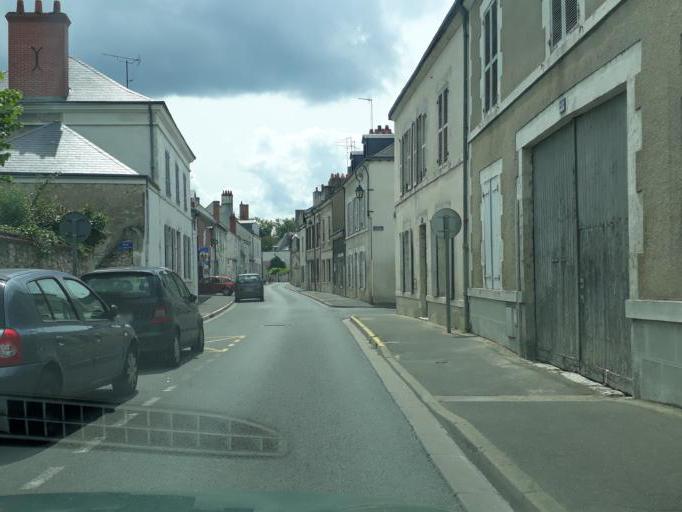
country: FR
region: Centre
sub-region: Departement du Loiret
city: Meung-sur-Loire
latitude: 47.8272
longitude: 1.6974
